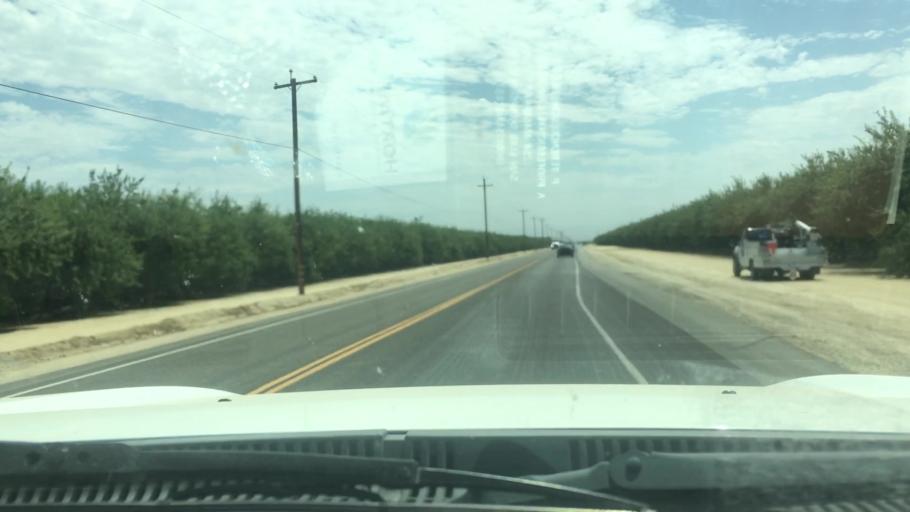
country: US
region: California
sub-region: Kern County
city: Wasco
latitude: 35.5580
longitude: -119.3211
